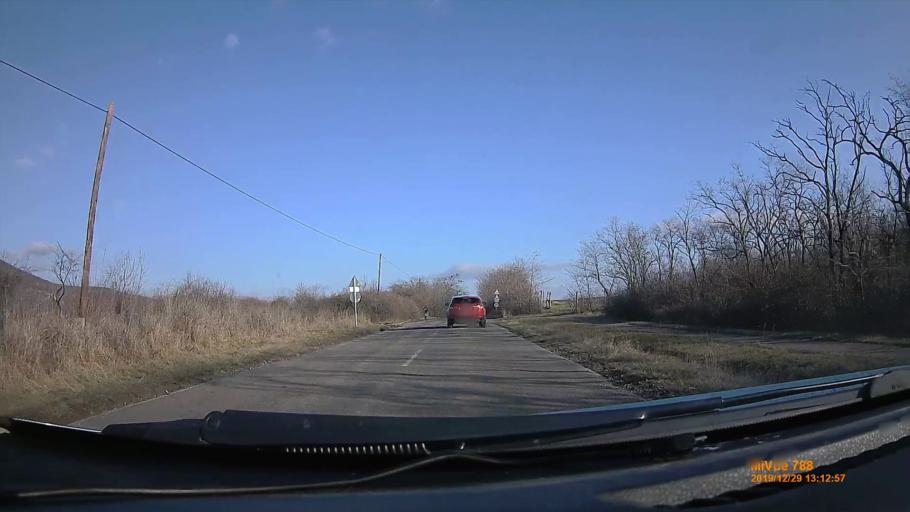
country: HU
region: Heves
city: Domoszlo
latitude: 47.8269
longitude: 20.0770
